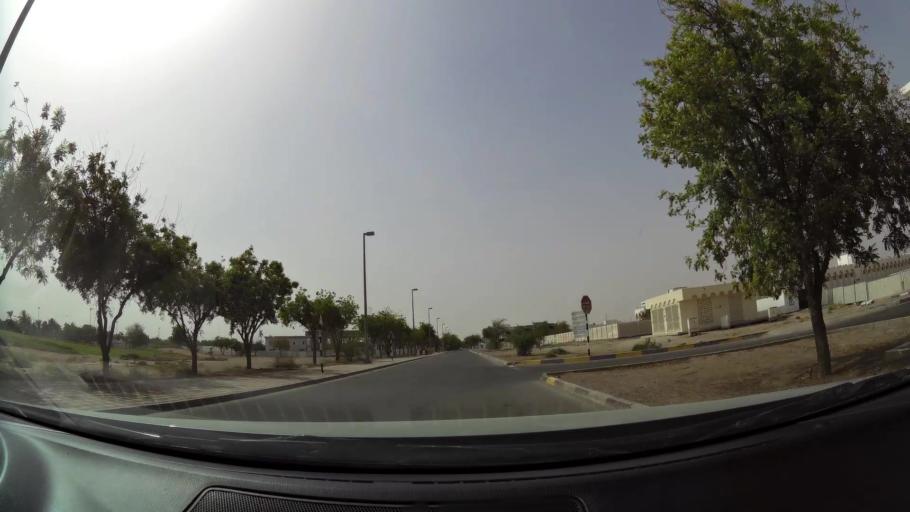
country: AE
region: Abu Dhabi
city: Al Ain
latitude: 24.1918
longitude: 55.6361
